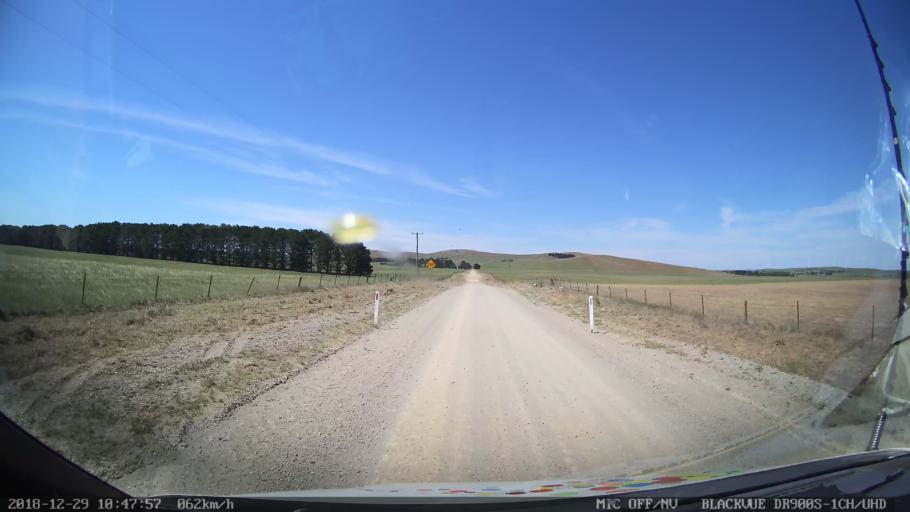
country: AU
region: New South Wales
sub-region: Palerang
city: Bungendore
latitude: -35.0639
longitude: 149.5155
